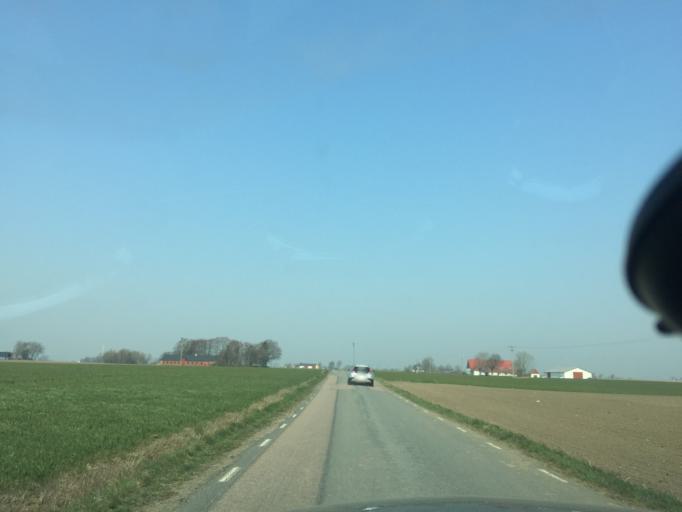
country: SE
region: Skane
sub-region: Simrishamns Kommun
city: Simrishamn
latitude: 55.4497
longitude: 14.2165
